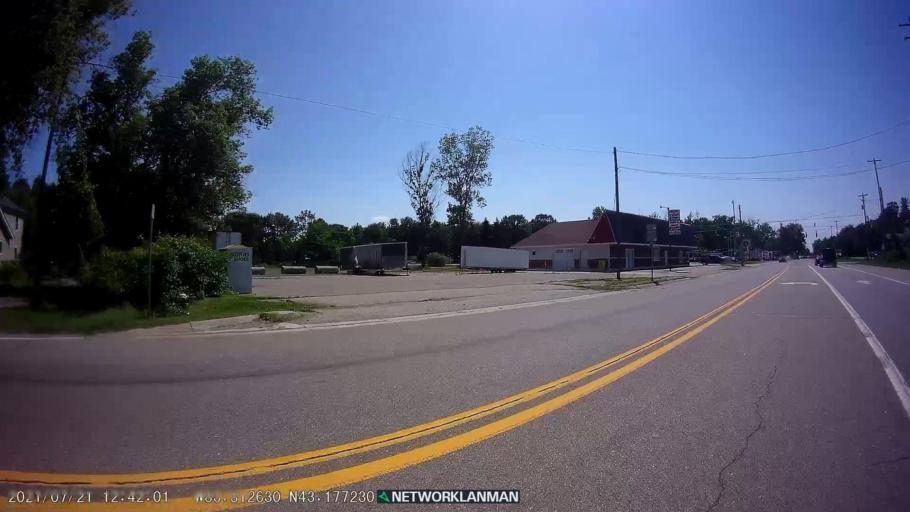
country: US
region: Michigan
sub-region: Saginaw County
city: Birch Run
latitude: 43.1775
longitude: -83.8125
